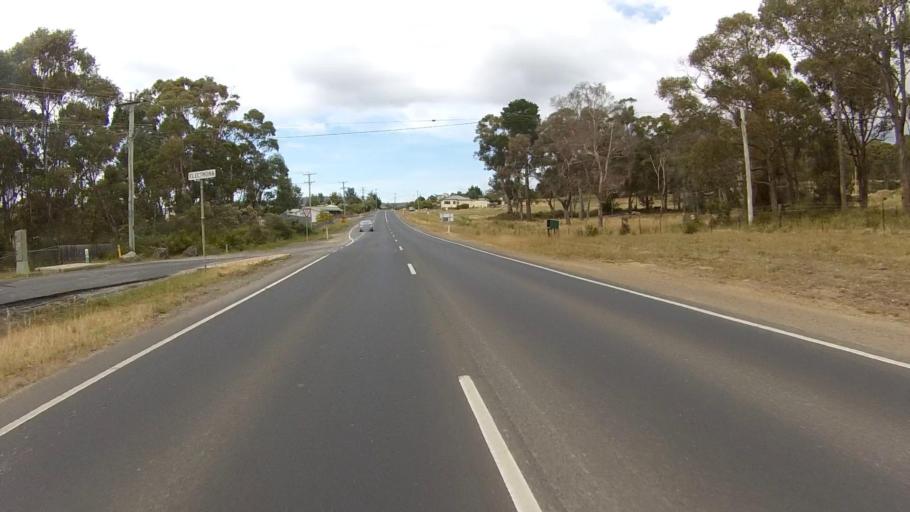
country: AU
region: Tasmania
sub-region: Kingborough
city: Margate
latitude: -43.0505
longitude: 147.2625
